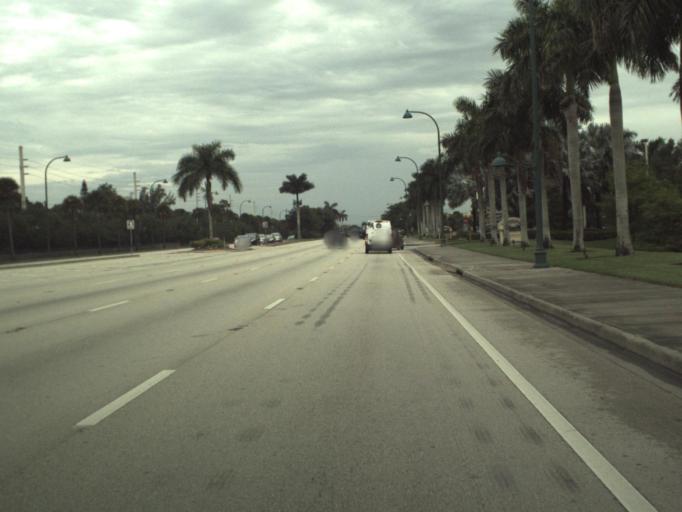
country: US
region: Florida
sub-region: Palm Beach County
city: Royal Palm Beach
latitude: 26.6811
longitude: -80.2220
